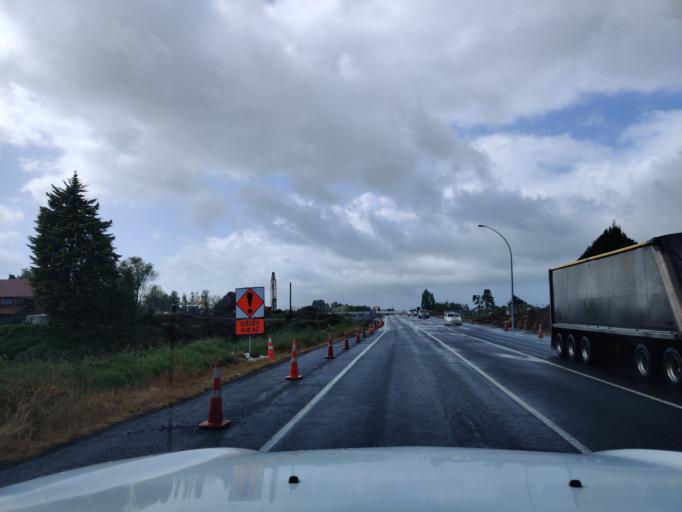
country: NZ
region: Waikato
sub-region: Hamilton City
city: Hamilton
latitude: -37.8130
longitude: 175.3406
